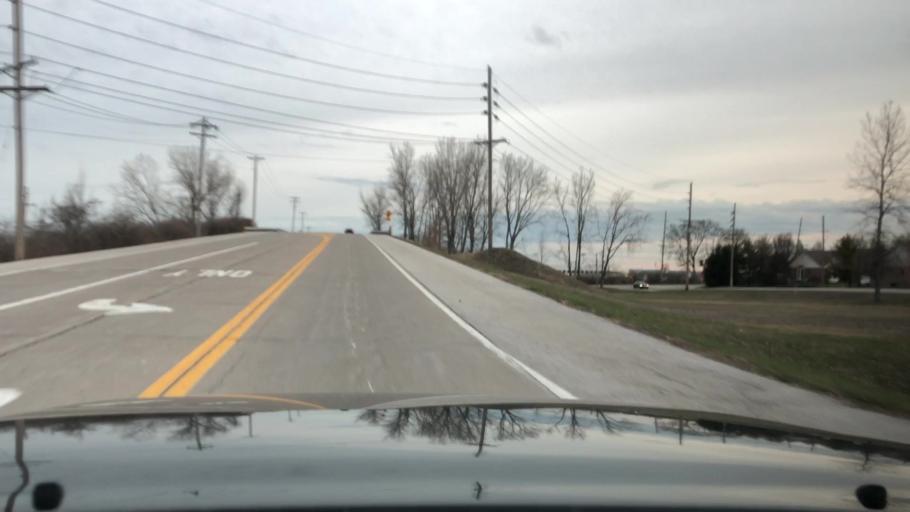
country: US
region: Missouri
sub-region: Saint Charles County
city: Saint Charles
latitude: 38.8156
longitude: -90.5121
